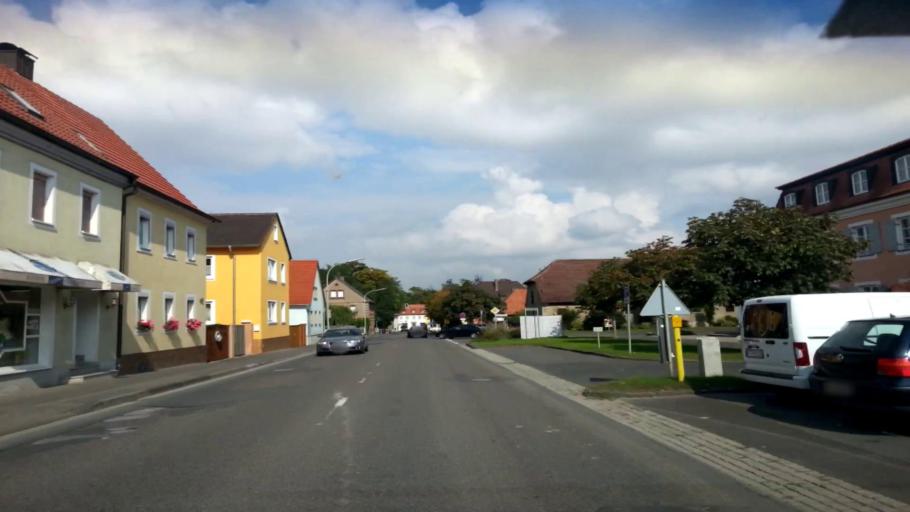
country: DE
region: Bavaria
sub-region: Regierungsbezirk Unterfranken
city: Wiesentheid
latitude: 49.7910
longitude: 10.3410
